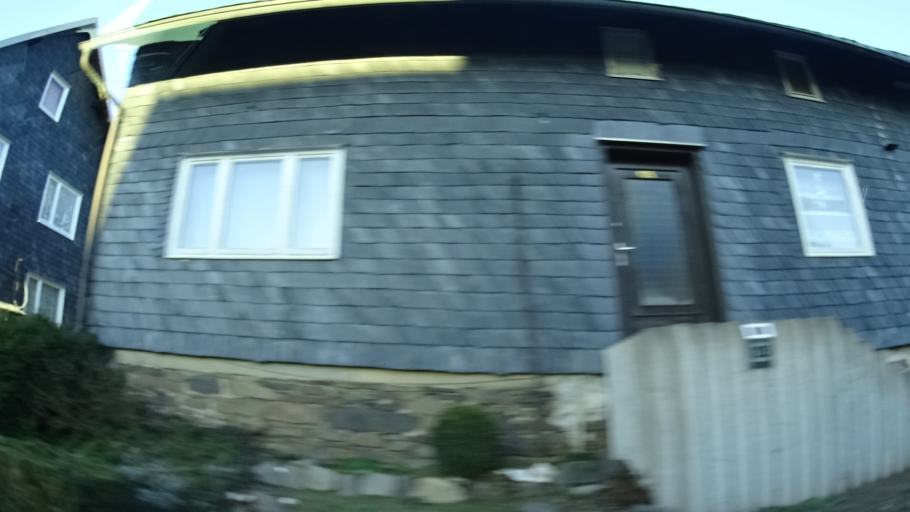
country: DE
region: Thuringia
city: Judenbach
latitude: 50.3954
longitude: 11.2196
